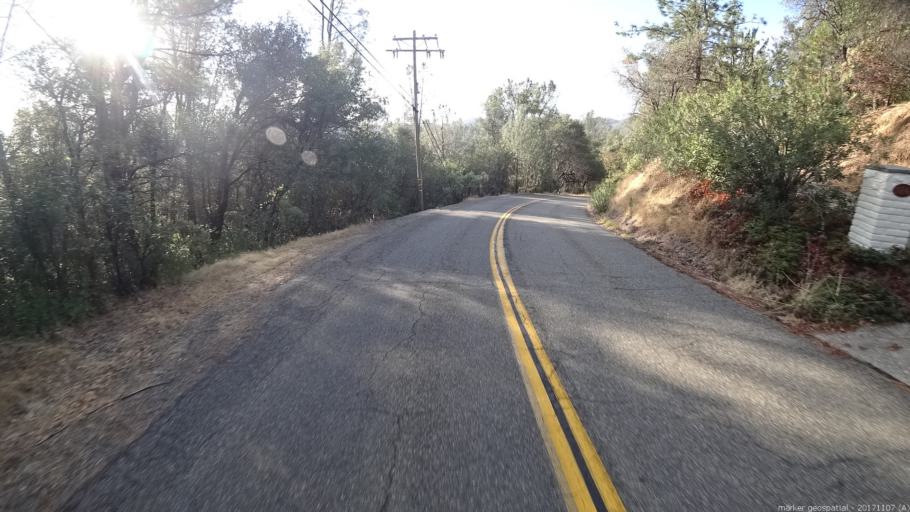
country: US
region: California
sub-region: Shasta County
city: Shasta
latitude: 40.5857
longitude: -122.4663
